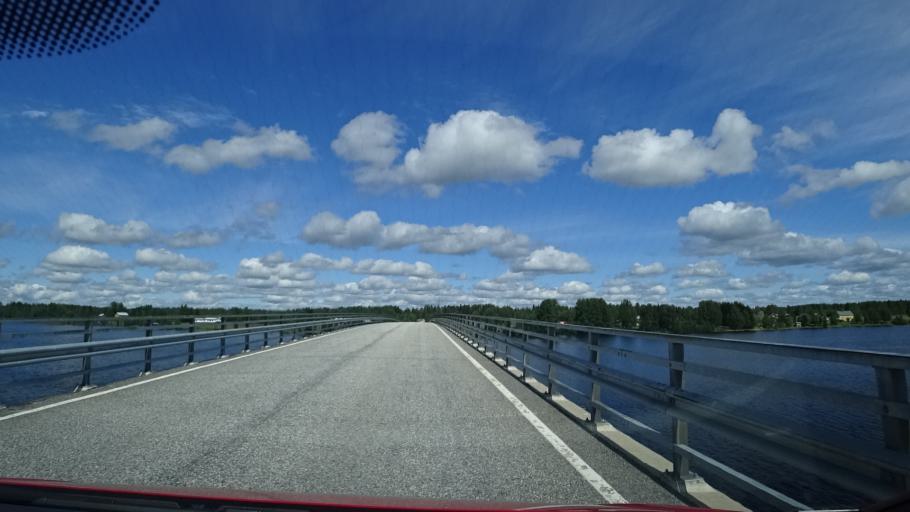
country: FI
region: Kainuu
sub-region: Kehys-Kainuu
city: Suomussalmi
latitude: 64.7405
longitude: 29.4393
